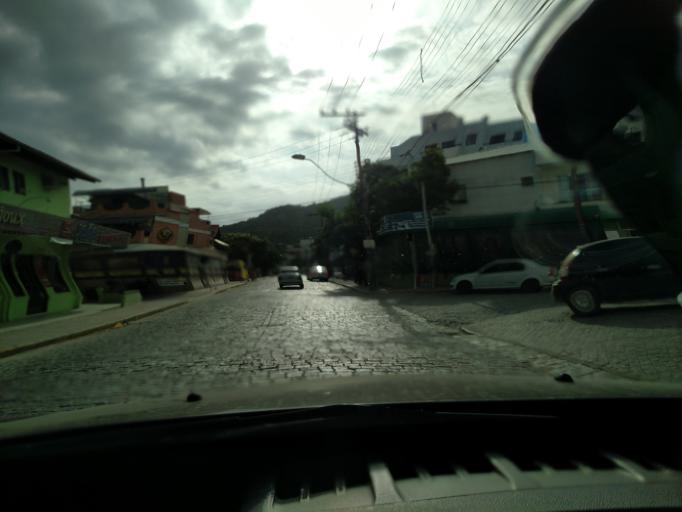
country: BR
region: Santa Catarina
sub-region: Porto Belo
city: Porto Belo
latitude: -27.1495
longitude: -48.4874
